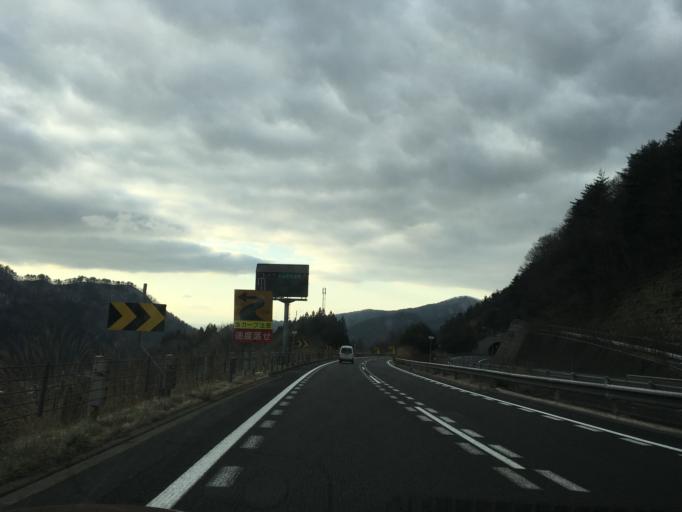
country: JP
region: Yamagata
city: Yamagata-shi
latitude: 38.2279
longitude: 140.4114
